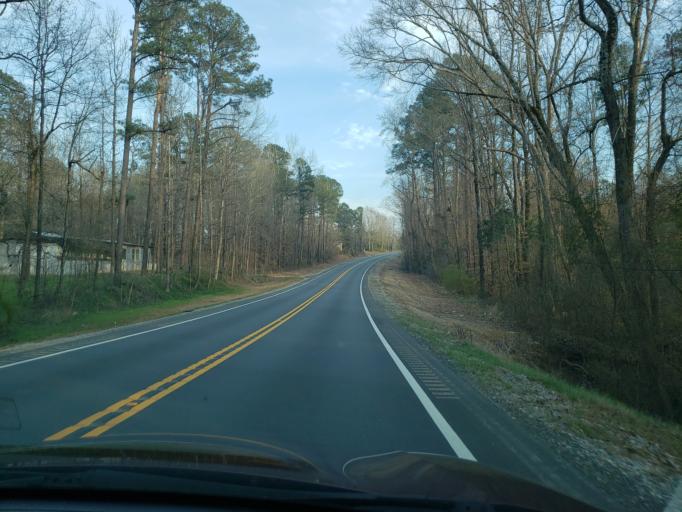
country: US
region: Alabama
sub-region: Hale County
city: Moundville
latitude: 32.8907
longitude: -87.6128
